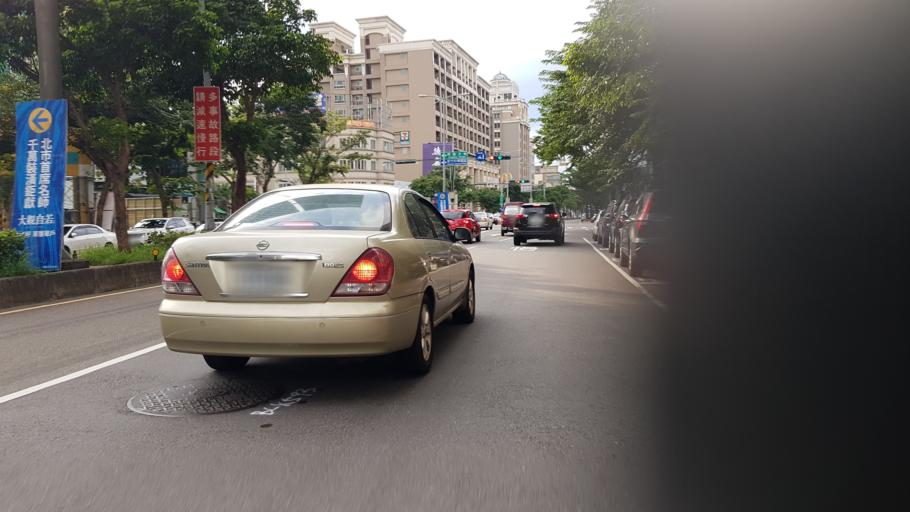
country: TW
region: Taiwan
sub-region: Hsinchu
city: Zhubei
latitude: 24.8083
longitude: 121.0335
